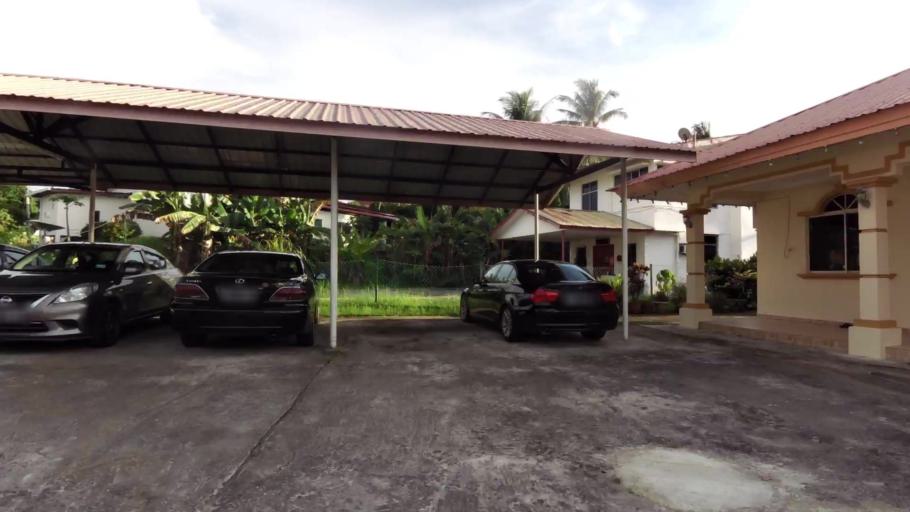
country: BN
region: Brunei and Muara
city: Bandar Seri Begawan
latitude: 4.9752
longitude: 114.9832
